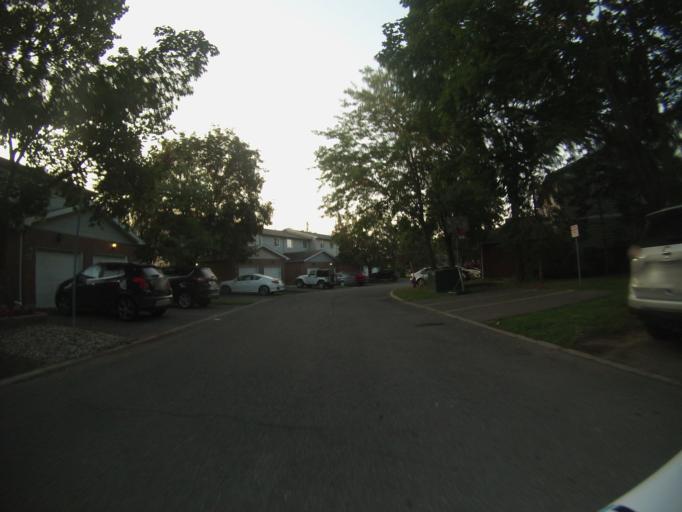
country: CA
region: Ontario
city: Ottawa
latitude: 45.3659
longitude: -75.6287
